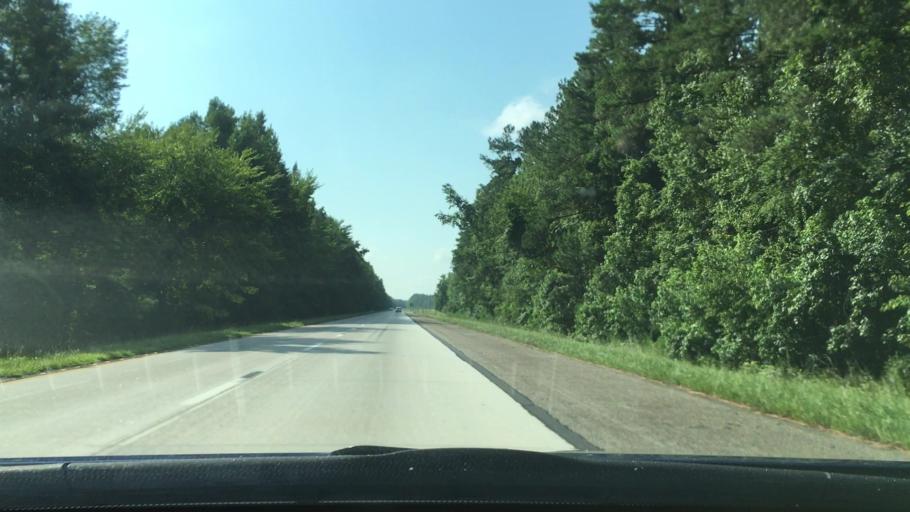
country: US
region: South Carolina
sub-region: Orangeburg County
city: Holly Hill
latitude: 33.2748
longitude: -80.4945
